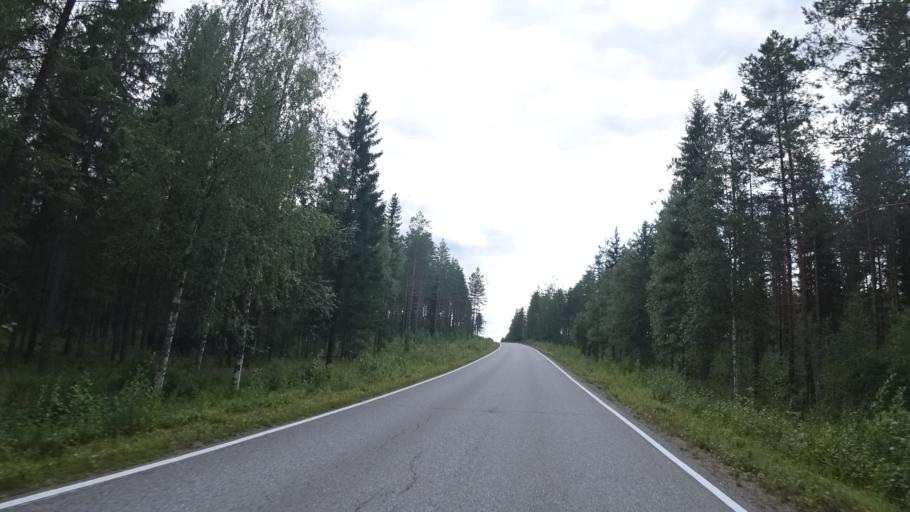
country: FI
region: North Karelia
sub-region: Joensuu
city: Ilomantsi
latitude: 62.4341
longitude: 31.0568
